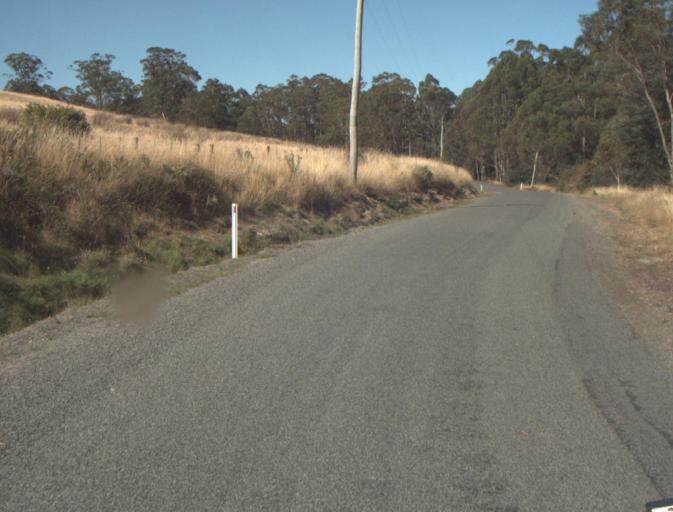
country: AU
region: Tasmania
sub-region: Launceston
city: Newstead
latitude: -41.3581
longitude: 147.3029
